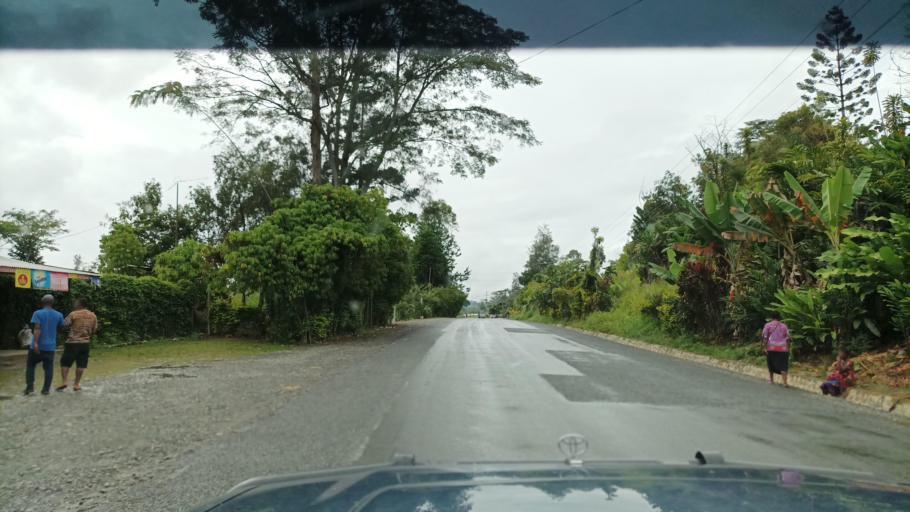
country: PG
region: Jiwaka
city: Minj
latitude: -5.8565
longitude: 144.6333
